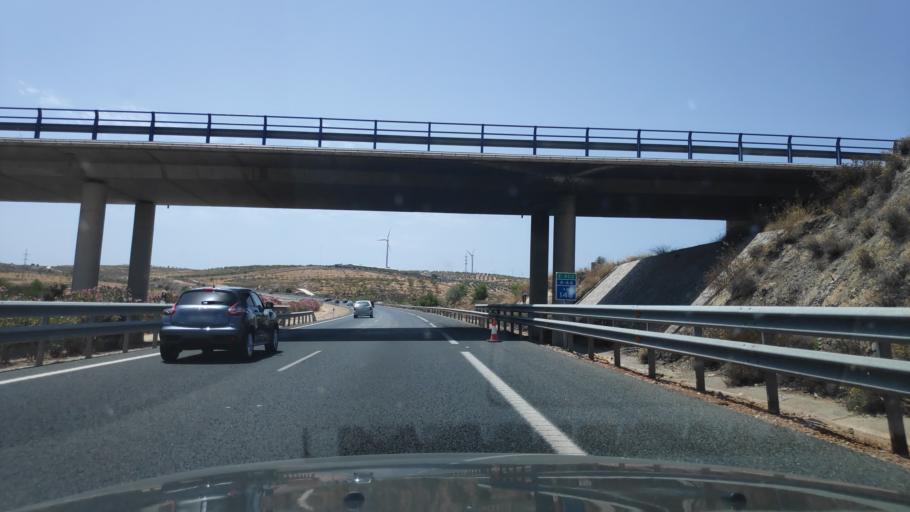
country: ES
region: Andalusia
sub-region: Provincia de Granada
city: Padul
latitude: 37.0132
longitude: -3.6405
